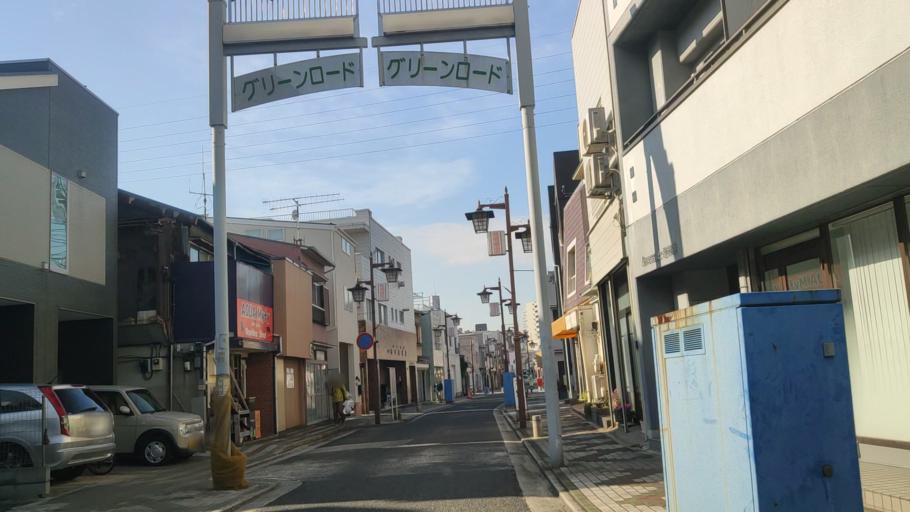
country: JP
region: Kanagawa
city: Yokohama
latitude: 35.4503
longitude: 139.6090
